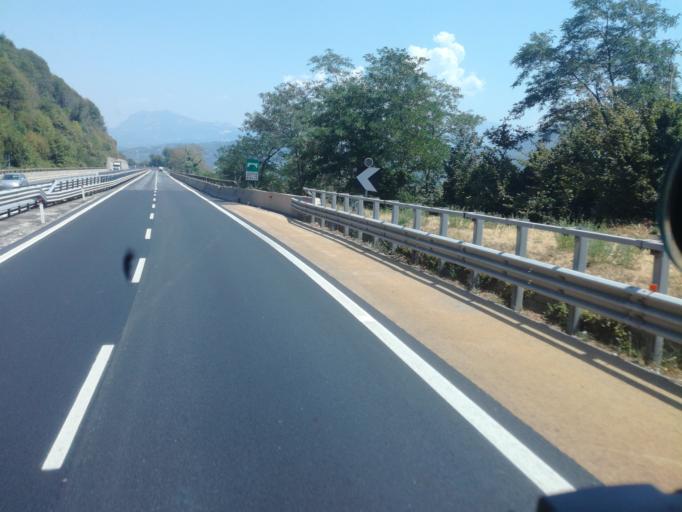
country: IT
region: Campania
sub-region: Provincia di Avellino
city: Monteforte Irpino
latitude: 40.8951
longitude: 14.7205
